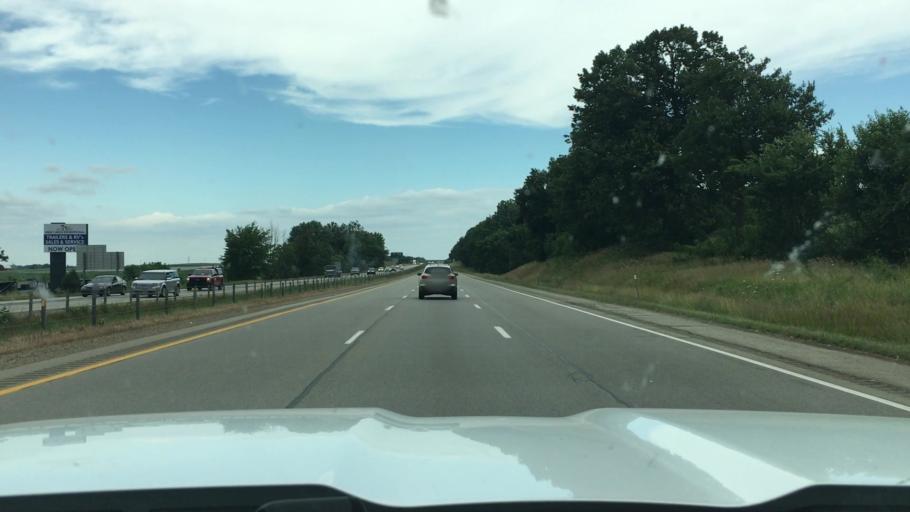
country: US
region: Michigan
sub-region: Allegan County
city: Wayland
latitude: 42.7290
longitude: -85.6731
